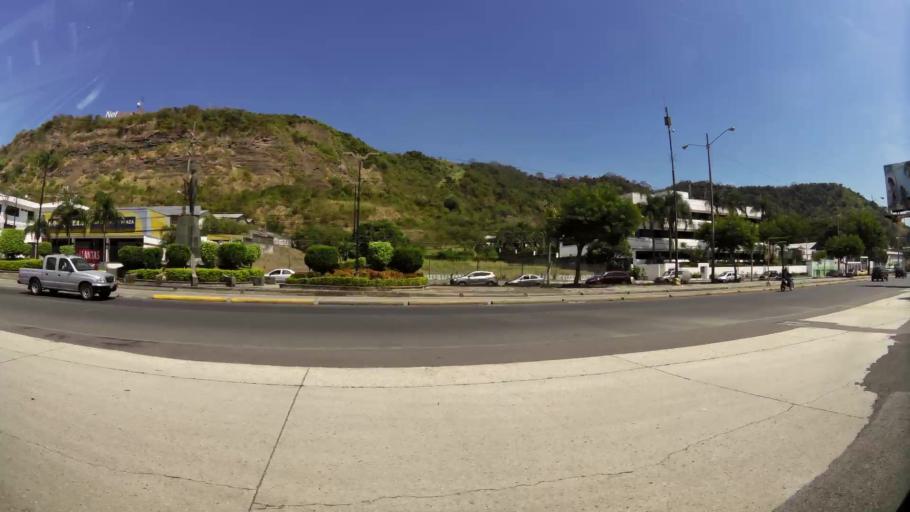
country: EC
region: Guayas
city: Guayaquil
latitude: -2.1706
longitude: -79.9175
